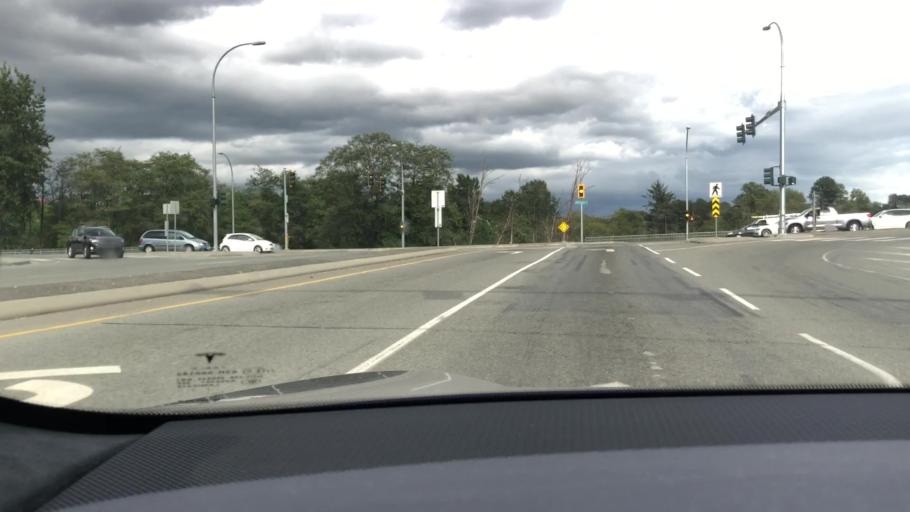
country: CA
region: British Columbia
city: Burnaby
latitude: 49.2590
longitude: -123.0050
